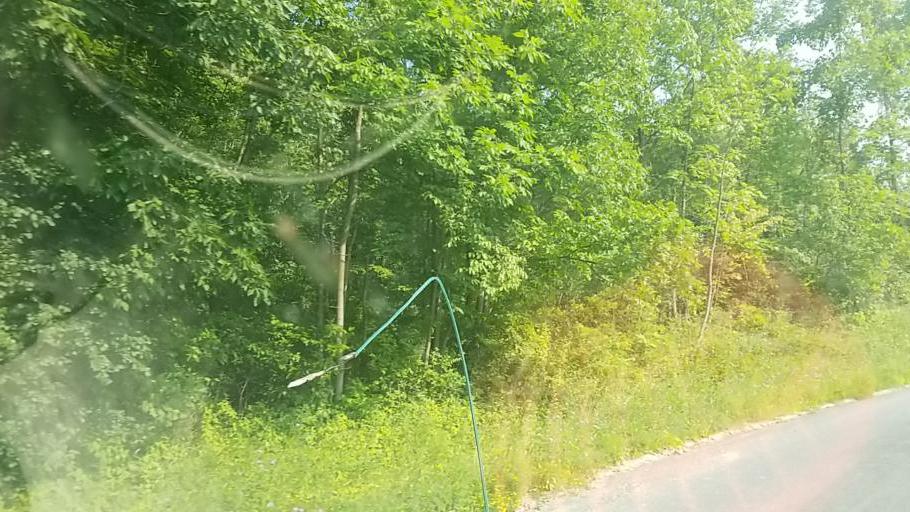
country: US
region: New York
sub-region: Montgomery County
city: Tribes Hill
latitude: 42.9232
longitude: -74.3269
